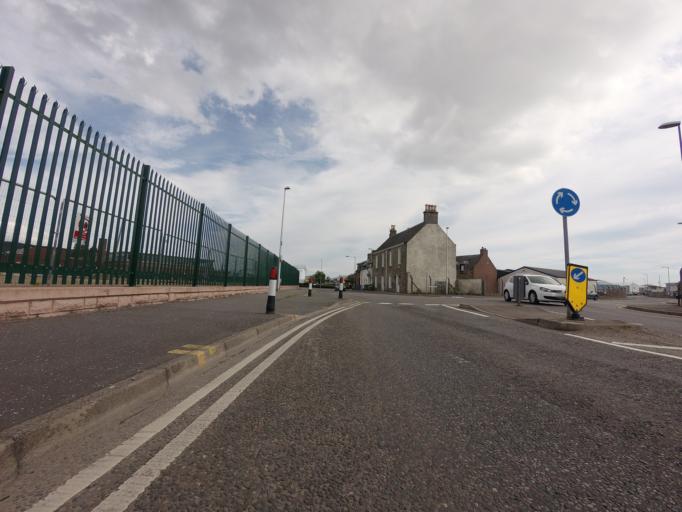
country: GB
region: Scotland
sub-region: Highland
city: Inverness
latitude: 57.4858
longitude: -4.2290
